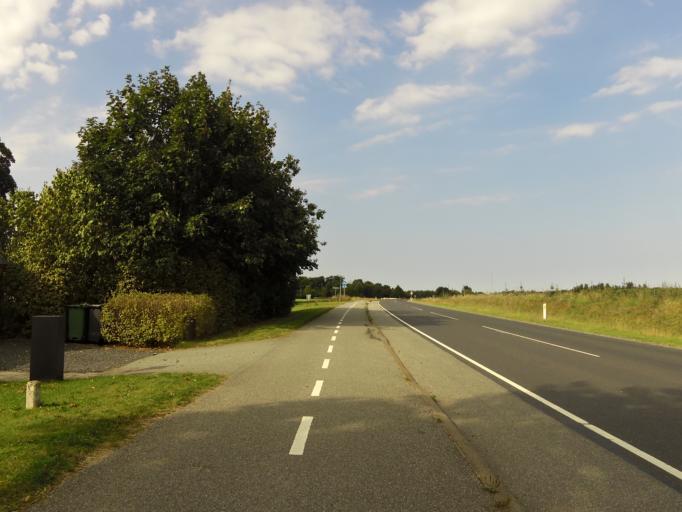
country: DK
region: South Denmark
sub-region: Vejen Kommune
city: Vejen
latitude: 55.4541
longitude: 9.1344
